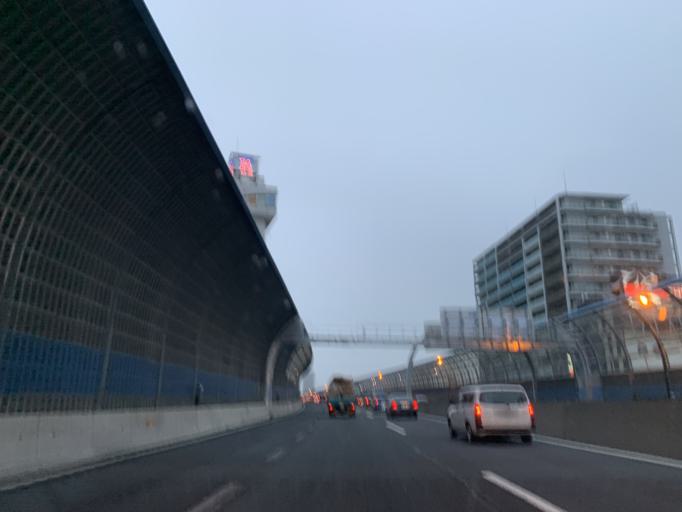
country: JP
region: Chiba
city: Funabashi
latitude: 35.6880
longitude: 139.9977
